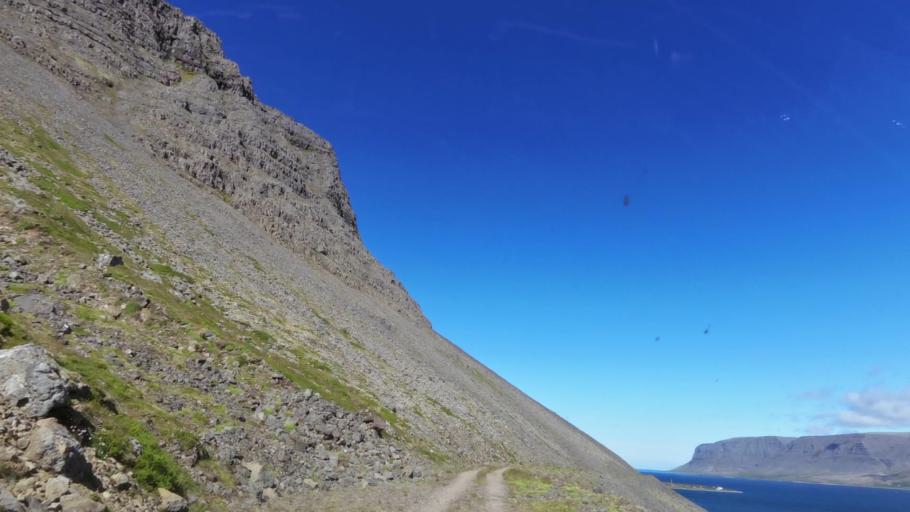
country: IS
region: West
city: Olafsvik
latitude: 65.6299
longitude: -23.9114
